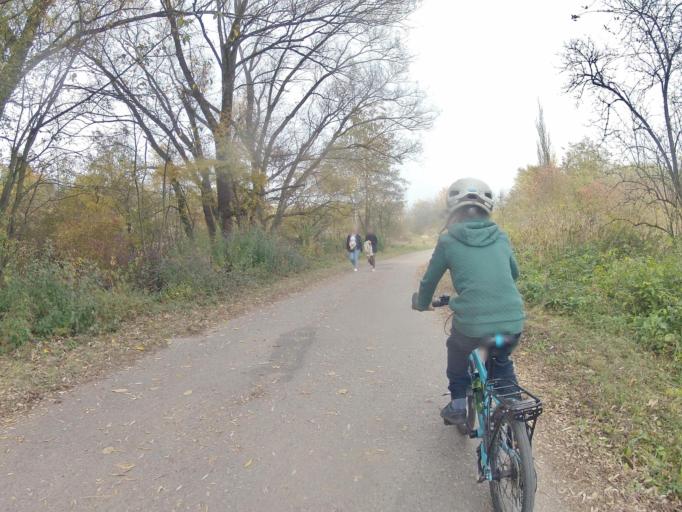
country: PL
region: Lesser Poland Voivodeship
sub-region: Krakow
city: Krakow
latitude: 50.0385
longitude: 19.9160
